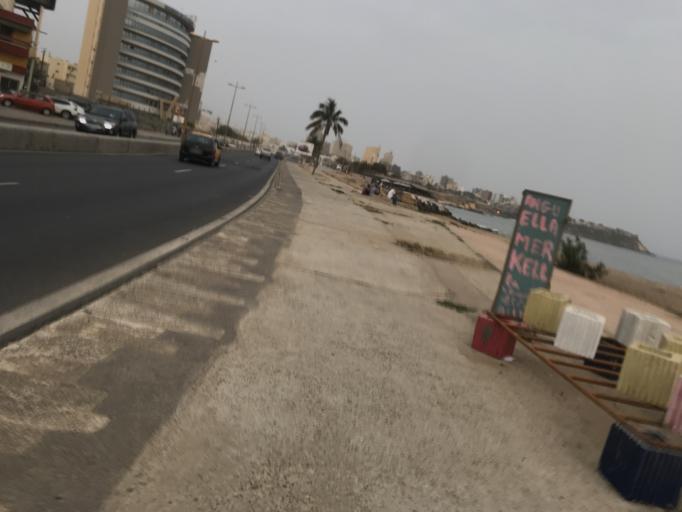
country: SN
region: Dakar
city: Dakar
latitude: 14.6745
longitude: -17.4526
